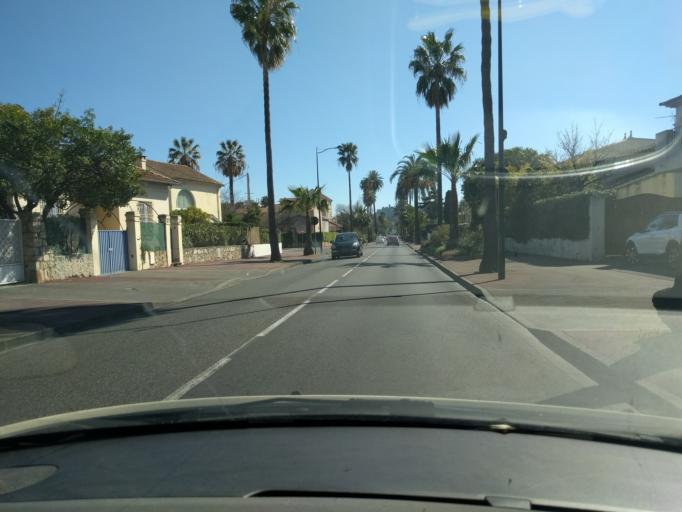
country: FR
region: Provence-Alpes-Cote d'Azur
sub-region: Departement du Var
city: Hyeres
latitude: 43.1167
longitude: 6.1227
